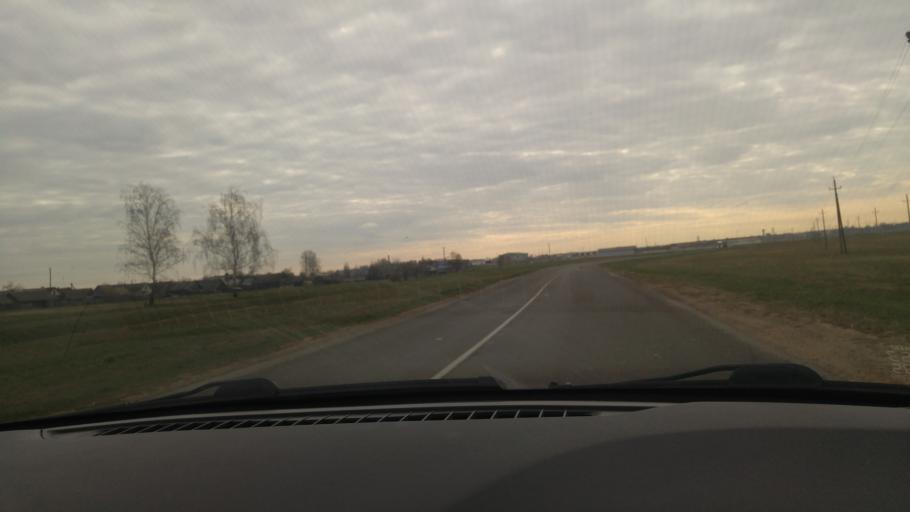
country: BY
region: Minsk
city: Chervyen'
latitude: 53.7175
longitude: 28.3823
